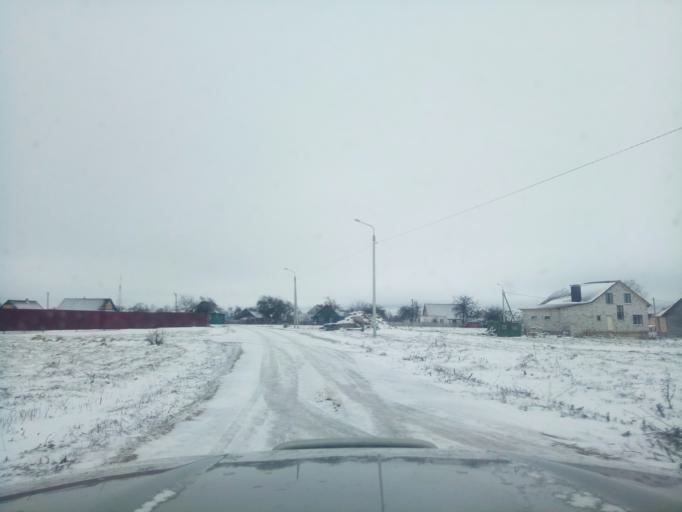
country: BY
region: Minsk
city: Kapyl'
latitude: 53.1611
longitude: 27.0786
